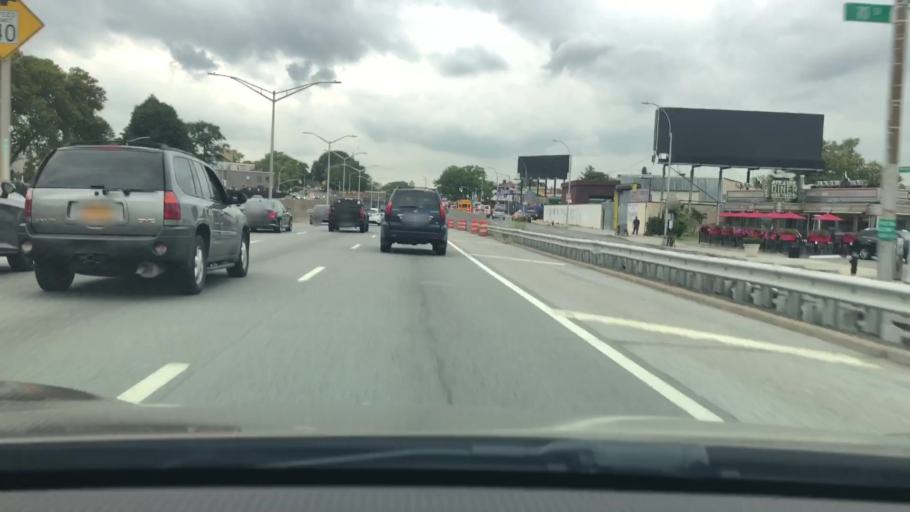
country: US
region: New York
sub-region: Queens County
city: Long Island City
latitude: 40.7660
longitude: -73.8994
